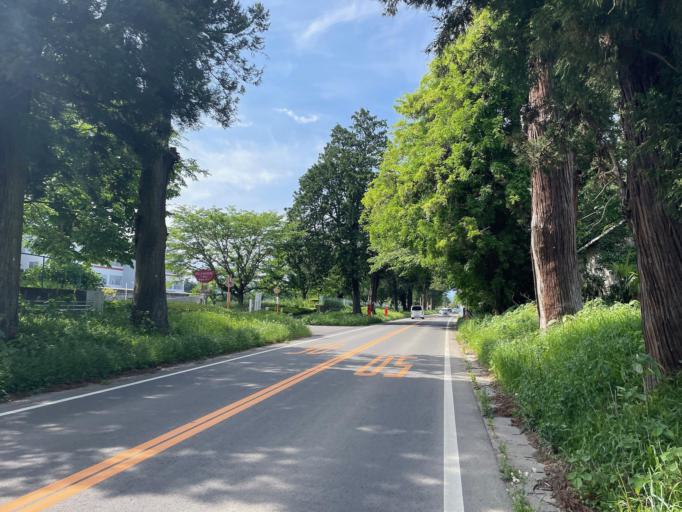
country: JP
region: Tochigi
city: Kanuma
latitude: 36.4883
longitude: 139.7591
